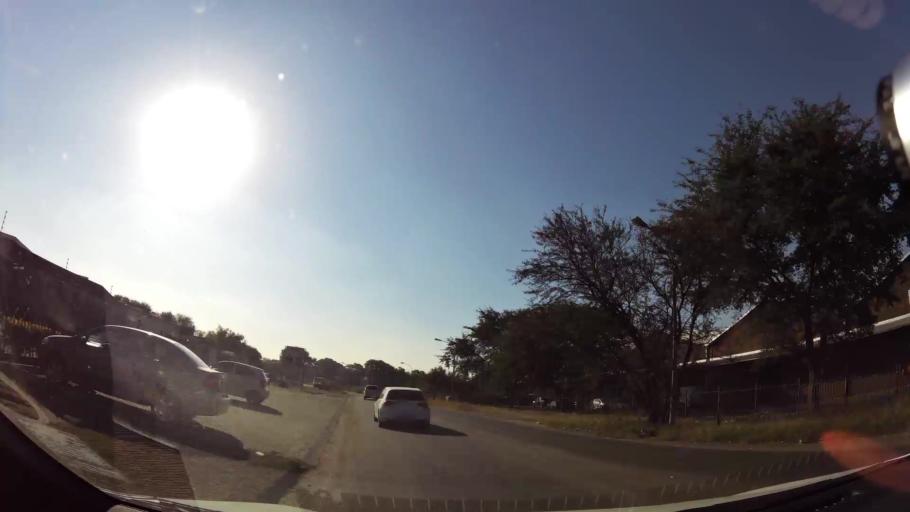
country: ZA
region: North-West
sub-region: Bojanala Platinum District Municipality
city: Rustenburg
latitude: -25.6655
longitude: 27.2614
